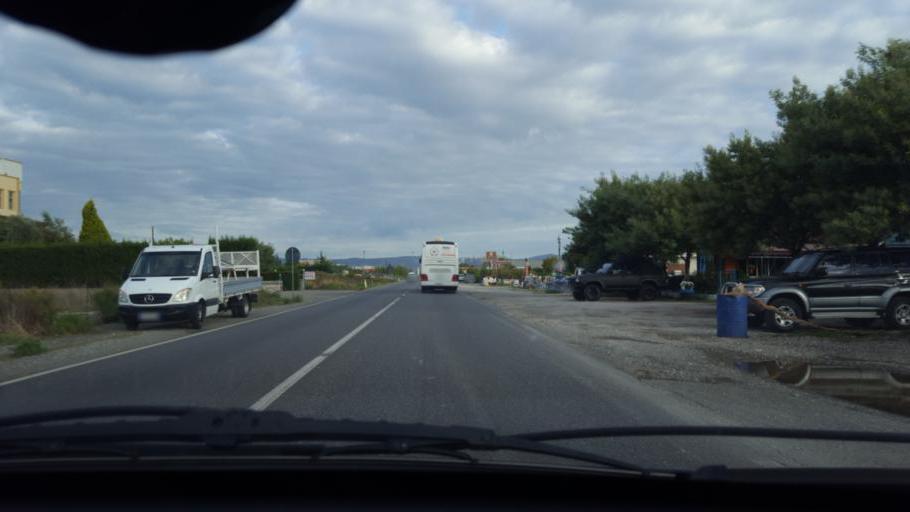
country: AL
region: Lezhe
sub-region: Rrethi i Lezhes
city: Shenkoll
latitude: 41.7358
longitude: 19.6536
